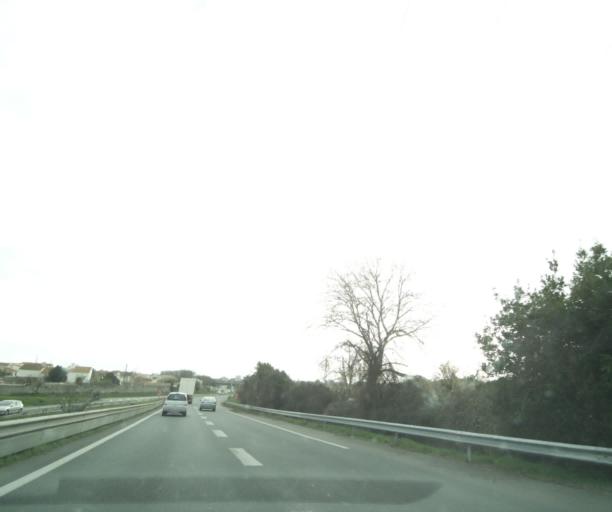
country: FR
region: Poitou-Charentes
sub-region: Departement de la Charente-Maritime
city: La Rochelle
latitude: 46.1697
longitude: -1.1907
